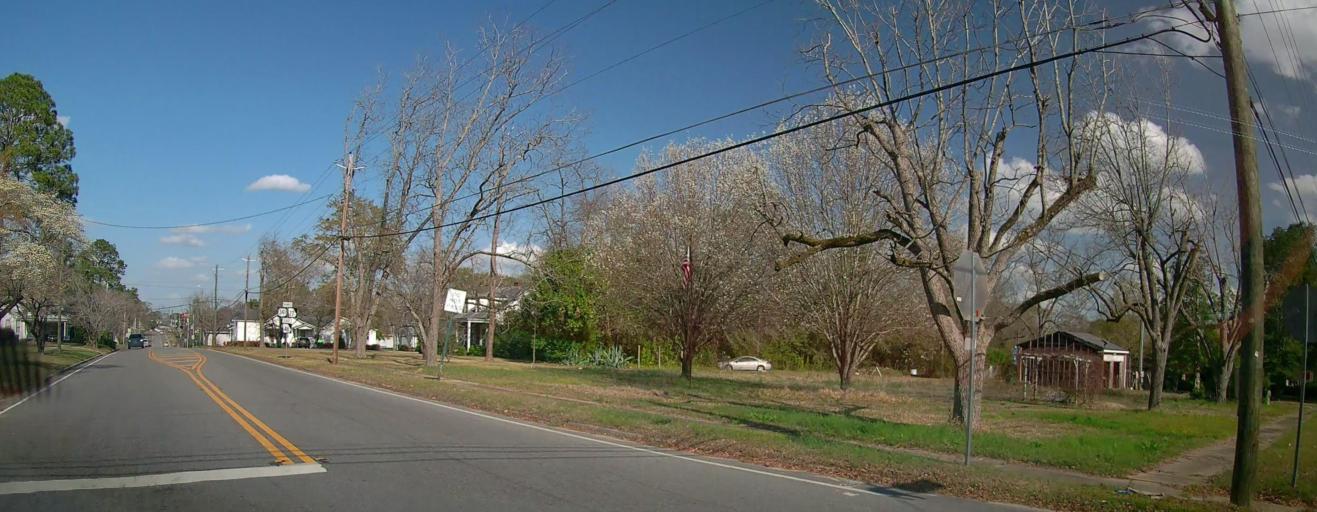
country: US
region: Georgia
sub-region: Dodge County
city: Eastman
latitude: 32.1941
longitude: -83.1829
